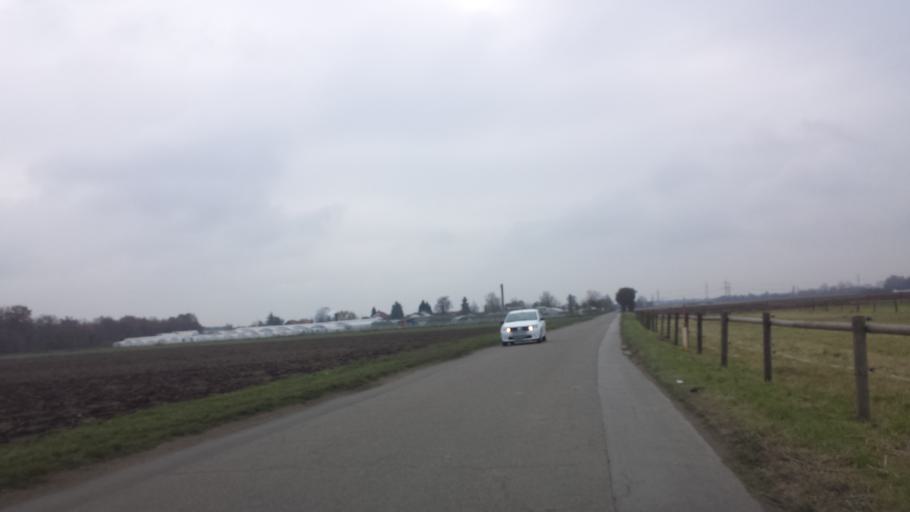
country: DE
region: Hesse
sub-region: Regierungsbezirk Darmstadt
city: Burstadt
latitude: 49.6261
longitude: 8.4801
